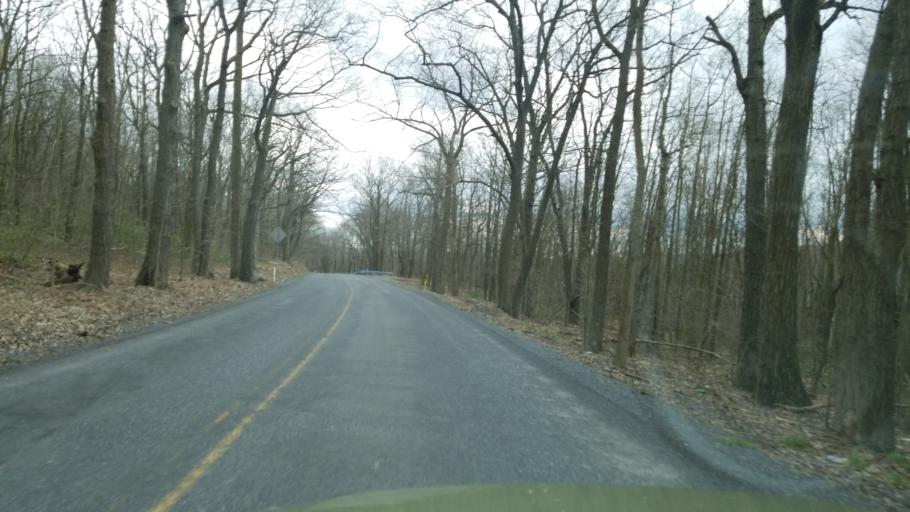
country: US
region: Pennsylvania
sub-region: Blair County
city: Tipton
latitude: 40.7224
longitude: -78.3533
